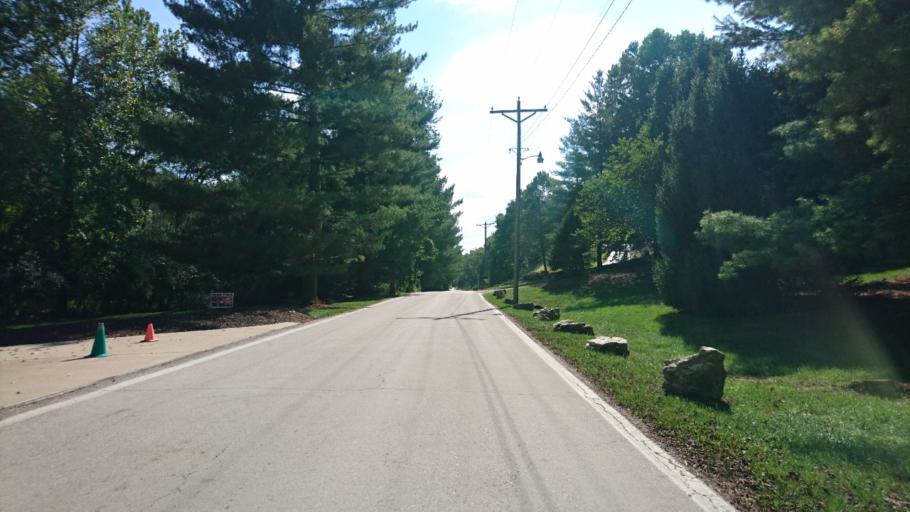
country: US
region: Missouri
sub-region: Saint Louis County
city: Wildwood
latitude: 38.5609
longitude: -90.6398
